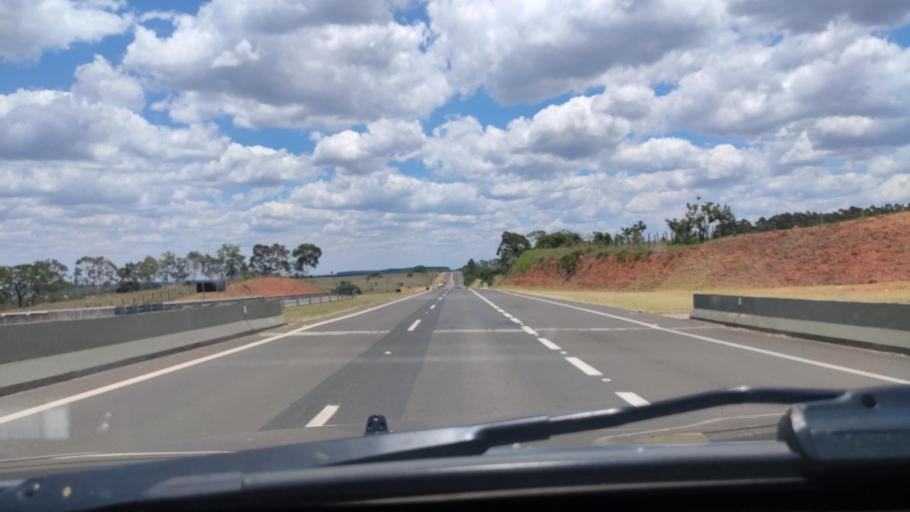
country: BR
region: Sao Paulo
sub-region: Duartina
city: Duartina
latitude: -22.4963
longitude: -49.2646
